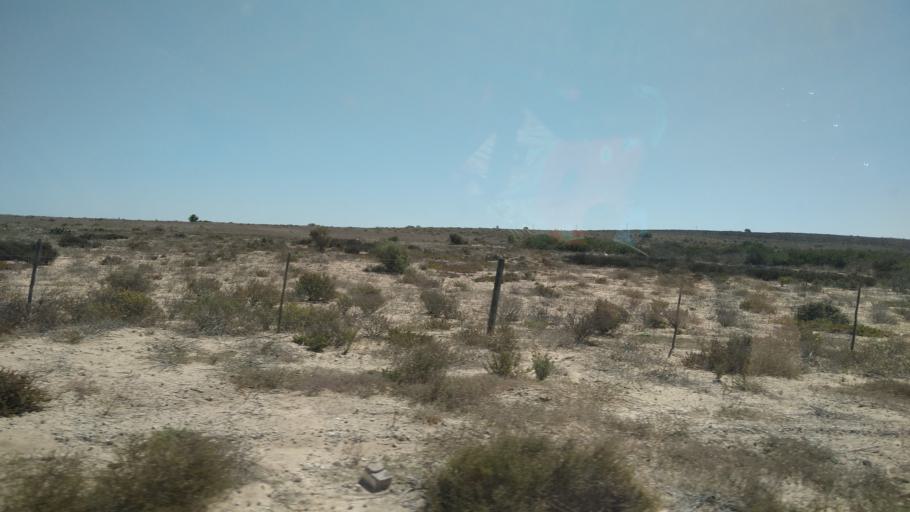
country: ZA
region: Western Cape
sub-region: West Coast District Municipality
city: Vredenburg
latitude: -33.0123
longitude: 18.1168
